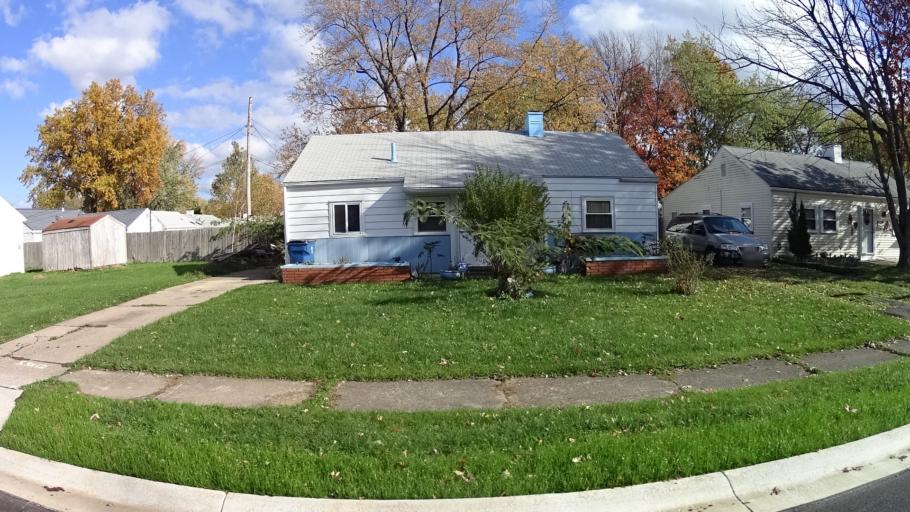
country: US
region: Ohio
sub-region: Lorain County
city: Sheffield
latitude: 41.4354
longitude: -82.1186
